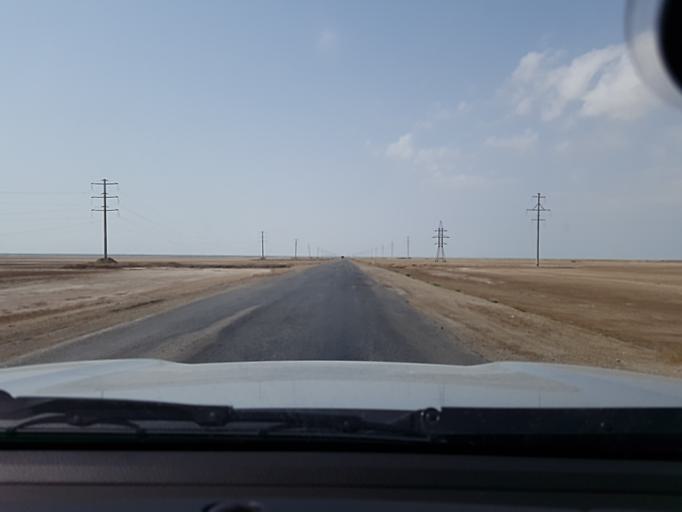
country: TM
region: Balkan
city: Gumdag
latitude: 39.0842
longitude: 54.5844
